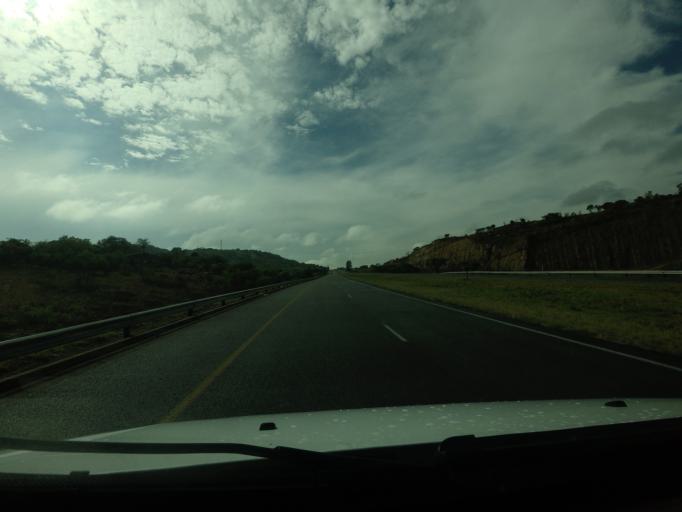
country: ZA
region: Gauteng
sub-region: City of Tshwane Metropolitan Municipality
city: Cullinan
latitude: -25.7801
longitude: 28.4761
